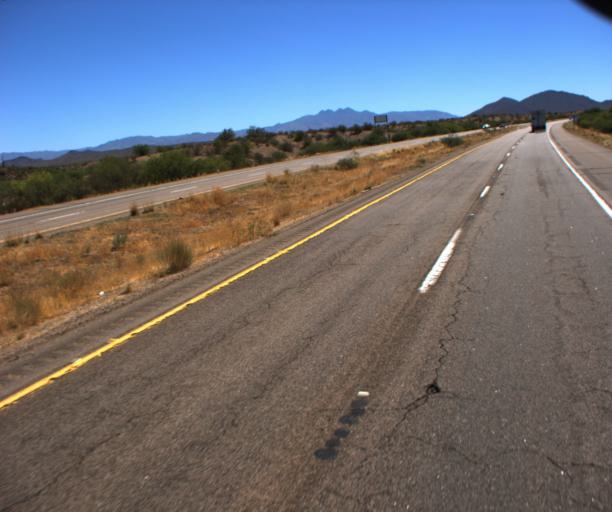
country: US
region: Arizona
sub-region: Maricopa County
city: Fountain Hills
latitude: 33.5824
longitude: -111.6597
